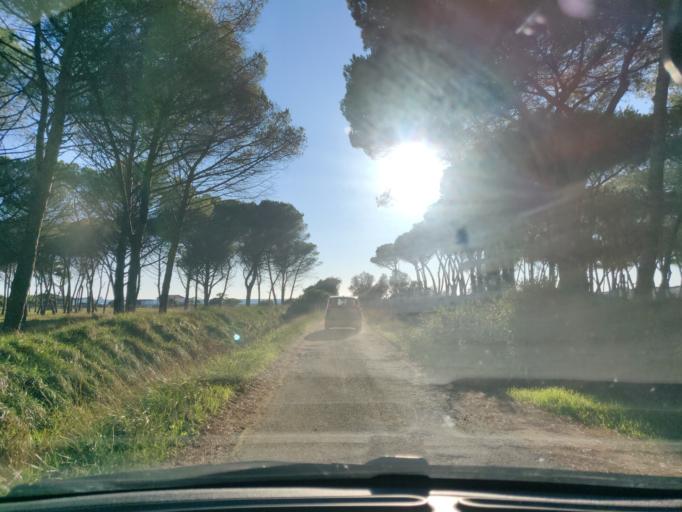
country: IT
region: Latium
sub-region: Citta metropolitana di Roma Capitale
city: Aurelia
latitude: 42.1489
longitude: 11.7456
